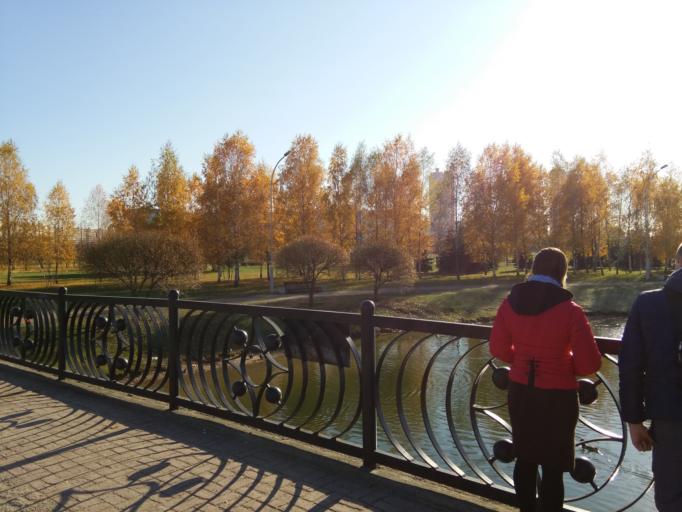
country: BY
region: Minsk
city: Borovlyany
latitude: 53.9453
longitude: 27.6790
